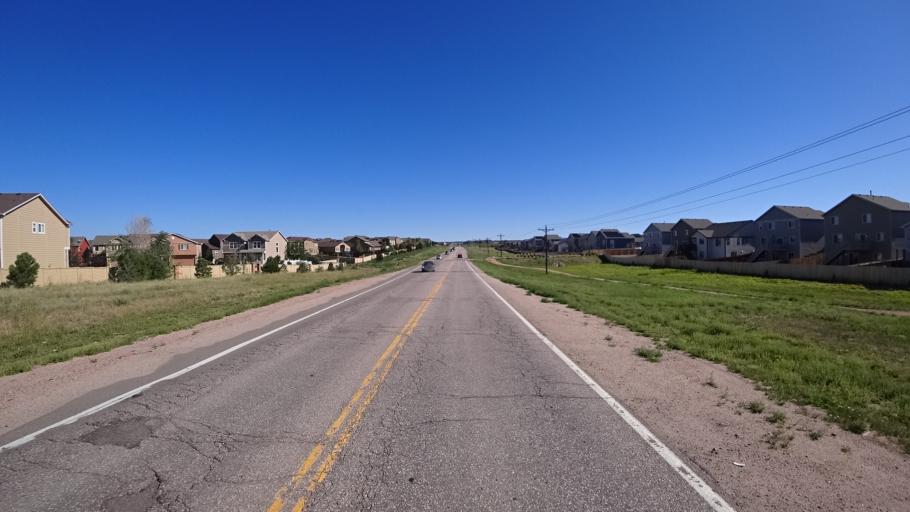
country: US
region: Colorado
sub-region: El Paso County
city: Cimarron Hills
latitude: 38.9179
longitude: -104.6828
